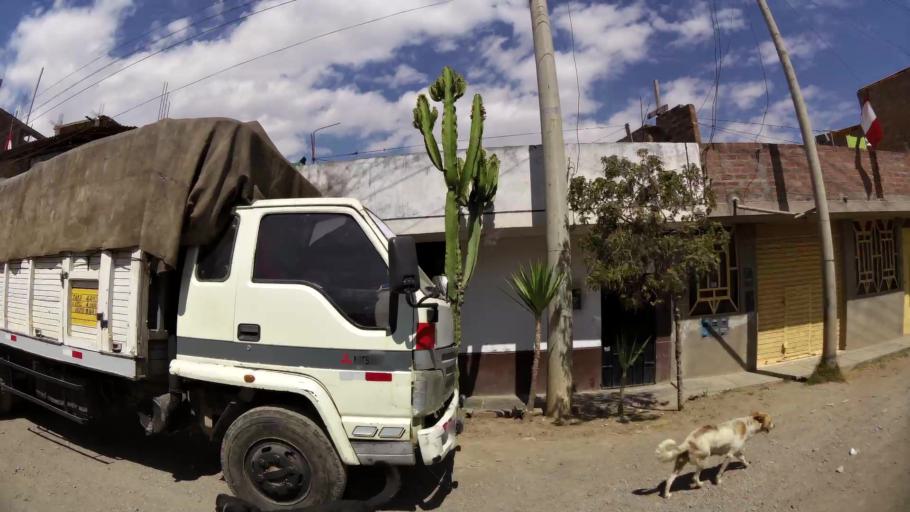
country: PE
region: Junin
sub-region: Provincia de Huancayo
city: El Tambo
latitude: -12.0673
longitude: -75.2228
